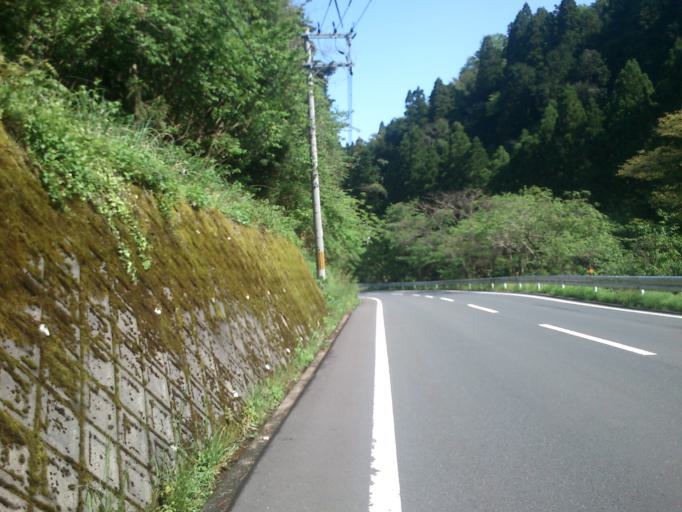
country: JP
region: Kyoto
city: Miyazu
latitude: 35.6447
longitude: 135.1294
